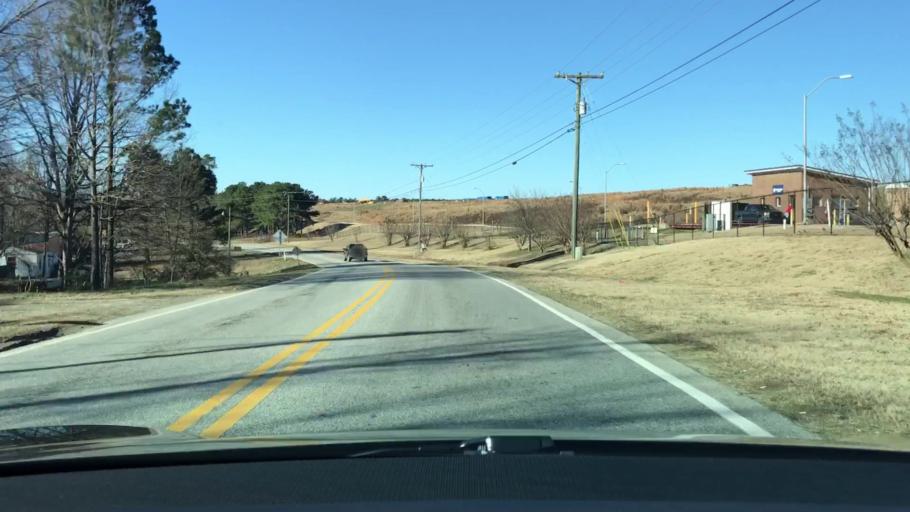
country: US
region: Georgia
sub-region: Barrow County
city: Winder
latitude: 33.9659
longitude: -83.7734
